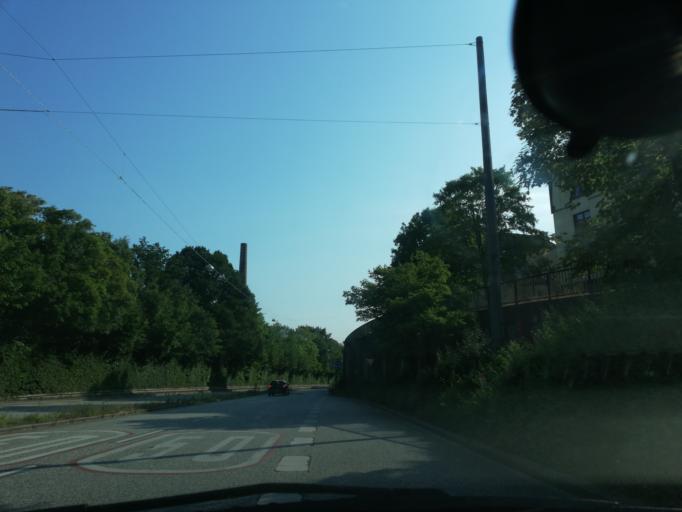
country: DE
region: North Rhine-Westphalia
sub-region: Regierungsbezirk Dusseldorf
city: Wuppertal
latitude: 51.2425
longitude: 7.1320
